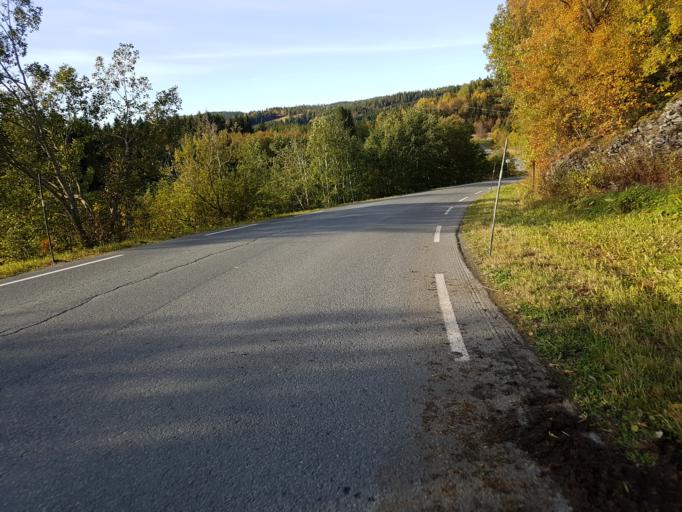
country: NO
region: Sor-Trondelag
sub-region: Klaebu
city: Klaebu
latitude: 63.3442
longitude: 10.5162
